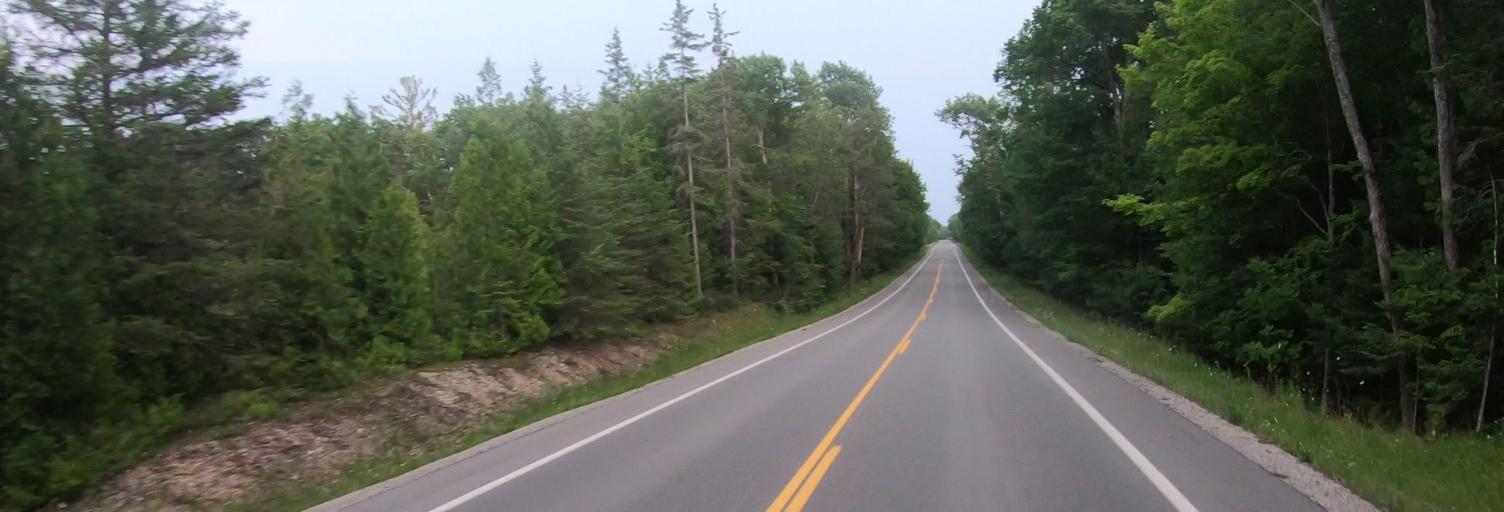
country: US
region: Michigan
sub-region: Mackinac County
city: Saint Ignace
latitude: 45.7747
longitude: -84.7732
